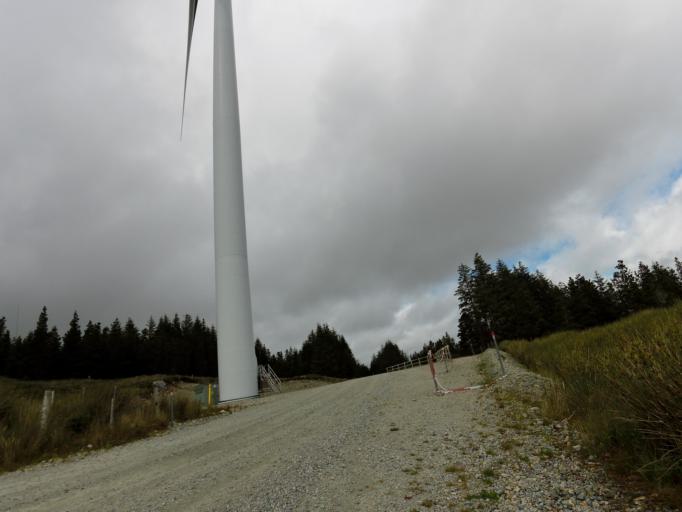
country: IE
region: Connaught
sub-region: County Galway
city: Oughterard
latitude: 53.3778
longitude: -9.3684
